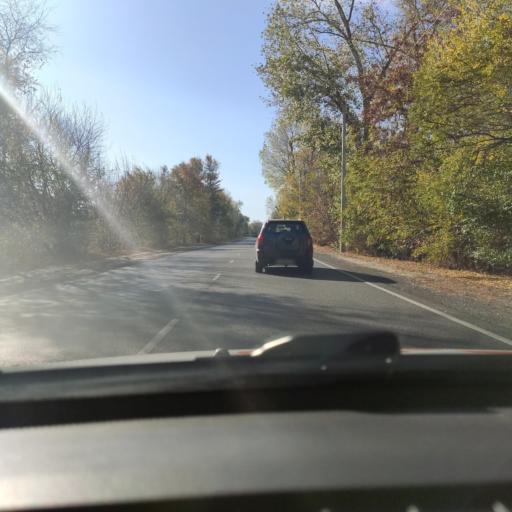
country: RU
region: Voronezj
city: Maslovka
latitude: 51.5916
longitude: 39.1752
